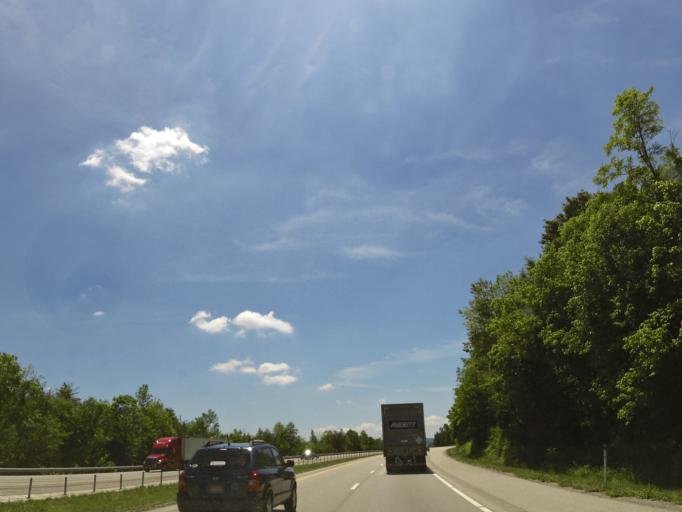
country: US
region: Tennessee
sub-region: Campbell County
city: Jellico
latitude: 36.6406
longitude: -84.1202
